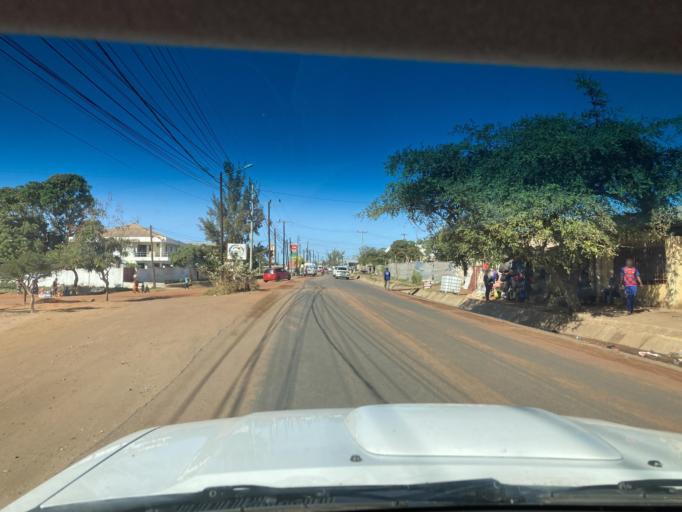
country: MZ
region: Cabo Delgado
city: Pemba
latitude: -12.9815
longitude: 40.5414
